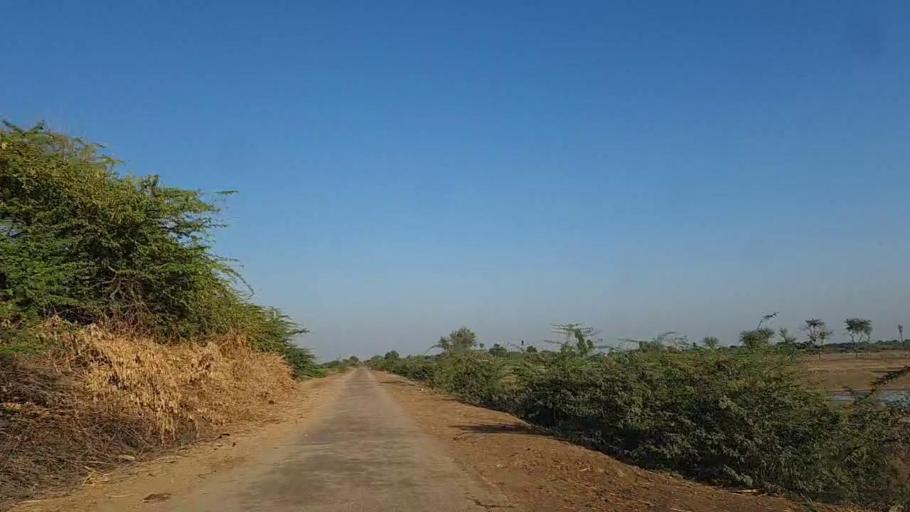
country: PK
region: Sindh
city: Samaro
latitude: 25.3469
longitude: 69.4187
